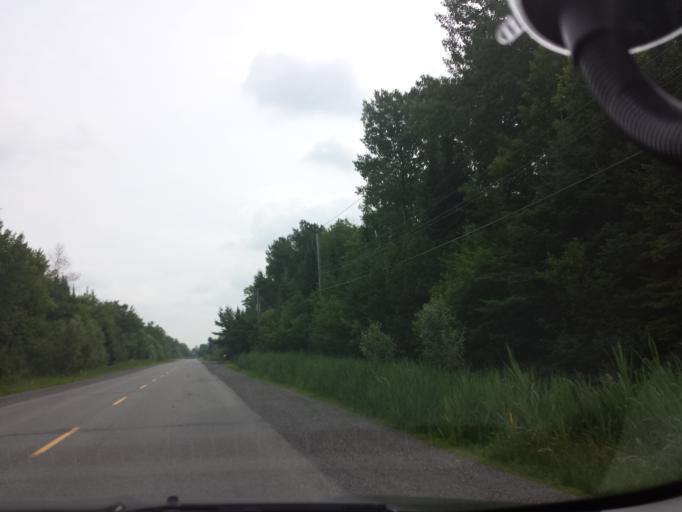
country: CA
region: Ontario
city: Ottawa
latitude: 45.3621
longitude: -75.5292
